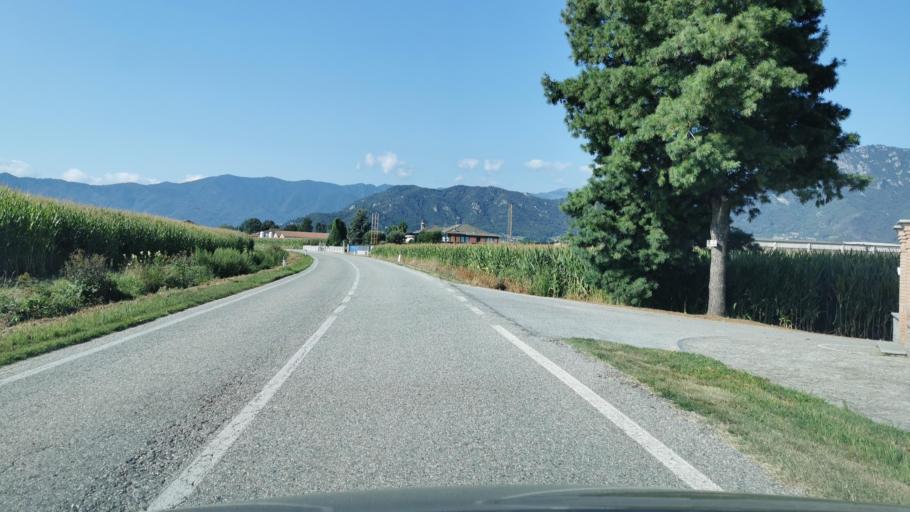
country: IT
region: Piedmont
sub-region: Provincia di Cuneo
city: Revello
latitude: 44.6849
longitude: 7.4147
